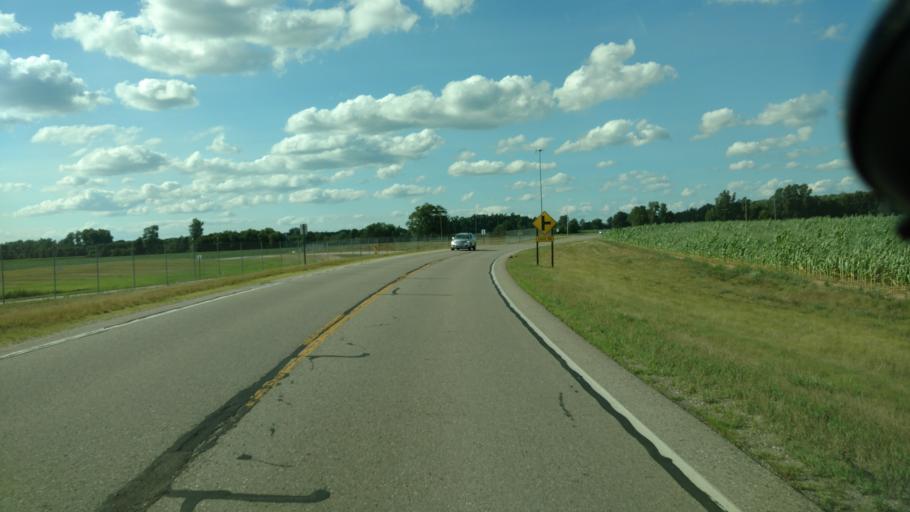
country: US
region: Michigan
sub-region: Ingham County
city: Edgemont Park
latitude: 42.7819
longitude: -84.5694
